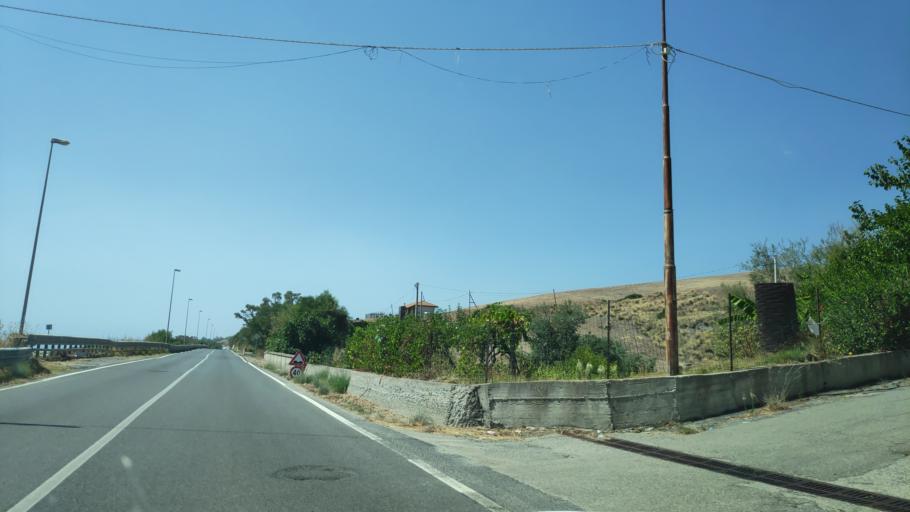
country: IT
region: Calabria
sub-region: Provincia di Reggio Calabria
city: Africo Nuovo
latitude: 38.0139
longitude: 16.1325
